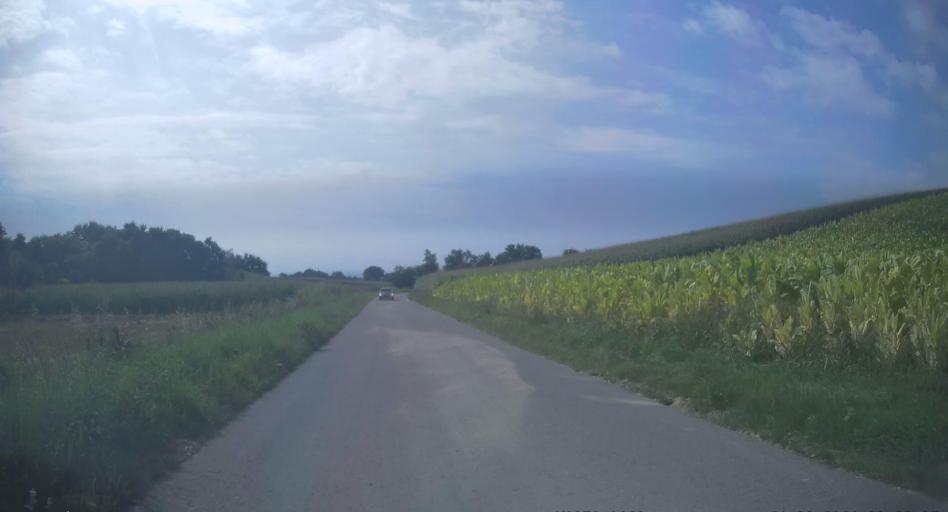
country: PL
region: Lesser Poland Voivodeship
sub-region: Powiat proszowicki
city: Nowe Brzesko
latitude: 50.1539
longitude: 20.4410
